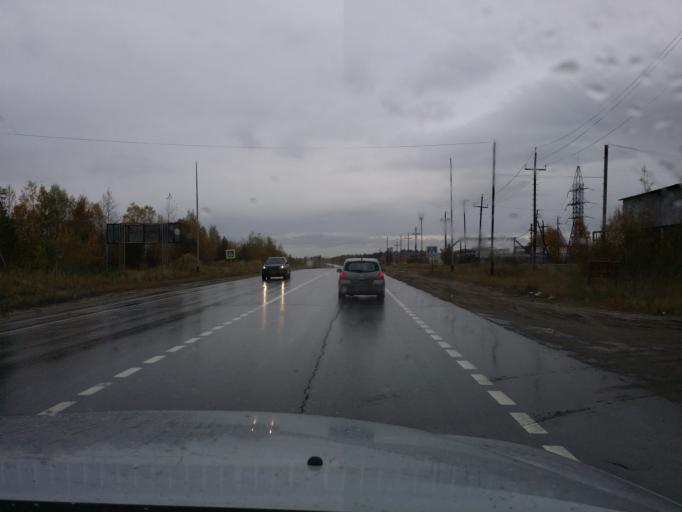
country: RU
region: Khanty-Mansiyskiy Avtonomnyy Okrug
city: Megion
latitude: 61.0539
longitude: 76.1132
